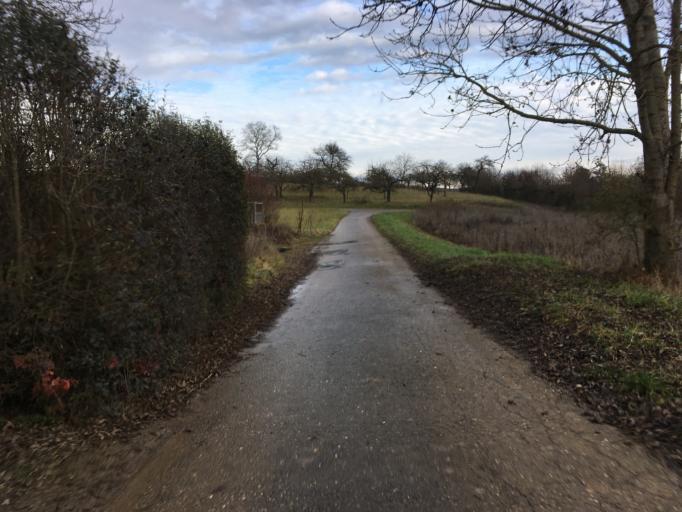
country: DE
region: Baden-Wuerttemberg
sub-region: Regierungsbezirk Stuttgart
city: Ilsfeld
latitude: 49.0546
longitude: 9.2242
